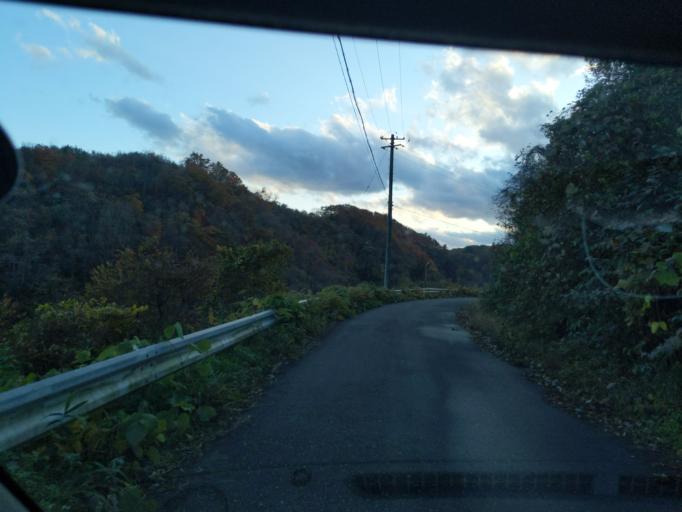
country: JP
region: Iwate
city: Ichinoseki
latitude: 39.0236
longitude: 141.0307
